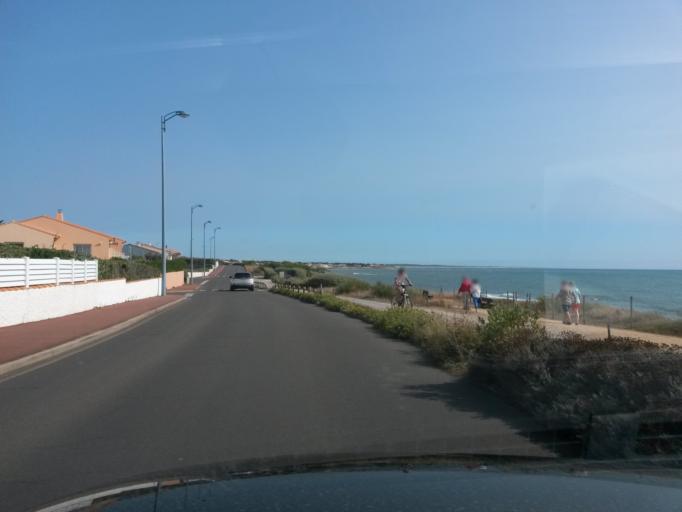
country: FR
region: Pays de la Loire
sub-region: Departement de la Vendee
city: Bretignolles-sur-Mer
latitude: 46.6331
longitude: -1.8866
